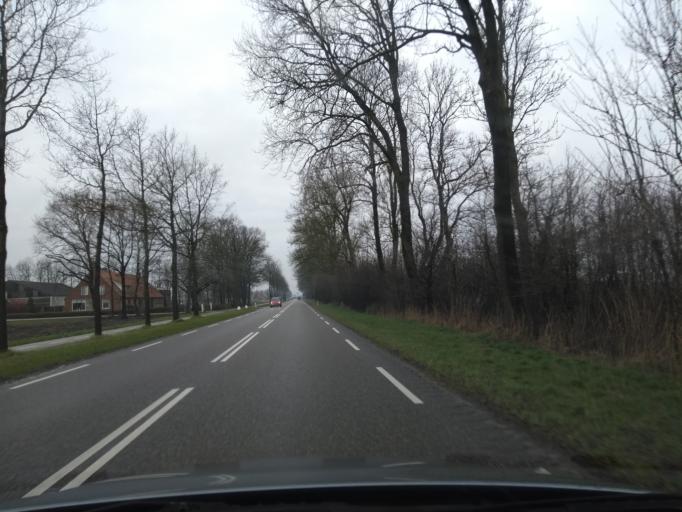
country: NL
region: Overijssel
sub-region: Gemeente Steenwijkerland
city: Vollenhove
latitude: 52.7071
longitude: 5.8843
